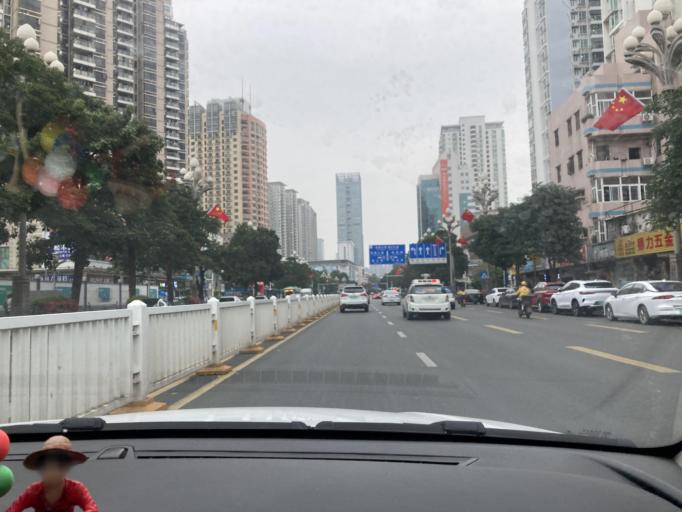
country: CN
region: Guangdong
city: Nantou
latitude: 22.5354
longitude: 113.9121
